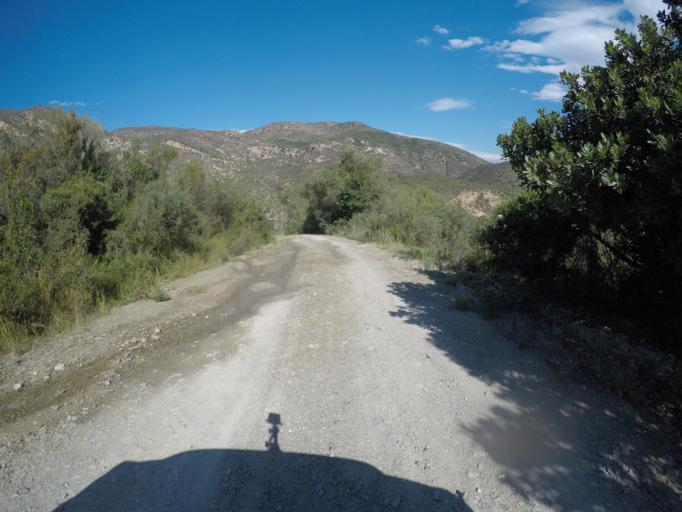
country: ZA
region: Eastern Cape
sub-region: Cacadu District Municipality
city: Kareedouw
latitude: -33.6462
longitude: 24.4562
